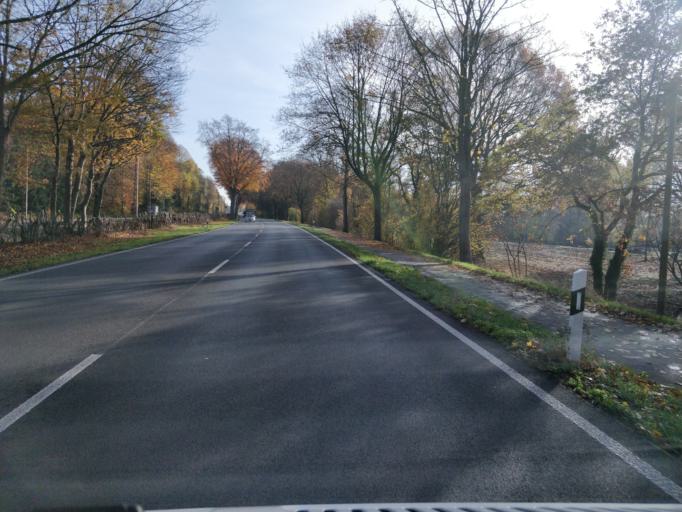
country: DE
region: North Rhine-Westphalia
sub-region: Regierungsbezirk Dusseldorf
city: Mehrhoog
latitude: 51.7608
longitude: 6.4732
